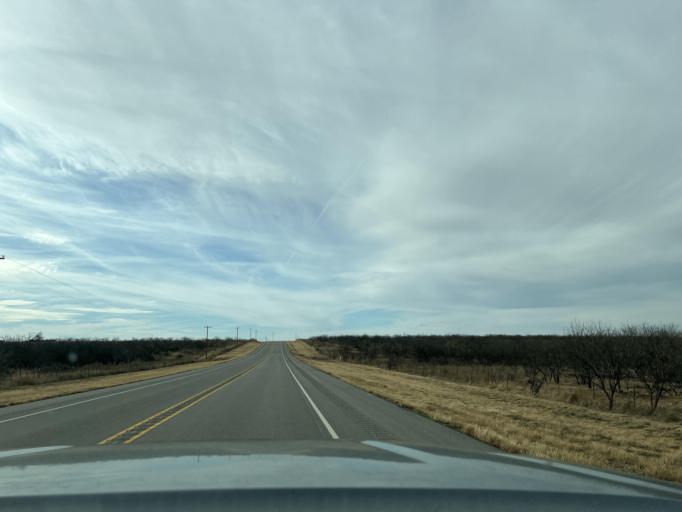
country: US
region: Texas
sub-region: Jones County
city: Anson
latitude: 32.7506
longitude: -99.6947
